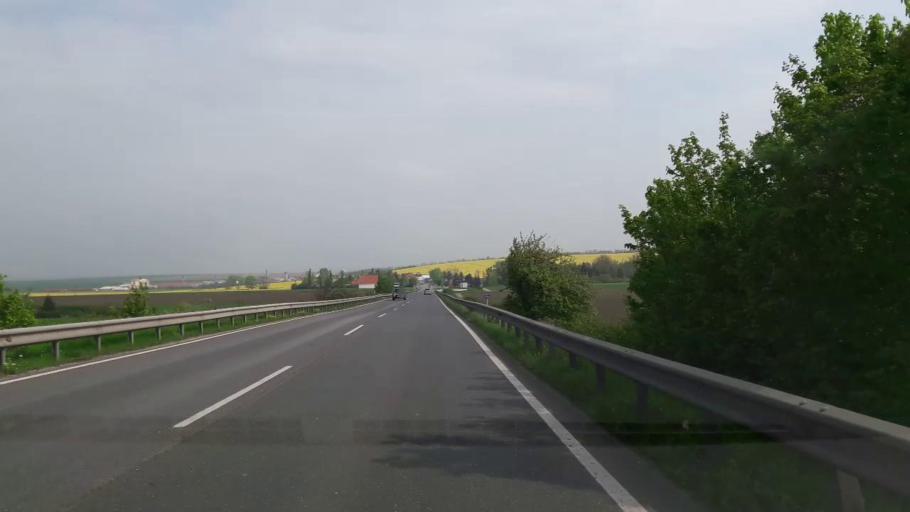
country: AT
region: Lower Austria
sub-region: Politischer Bezirk Hollabrunn
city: Haugsdorf
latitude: 48.7476
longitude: 16.0622
